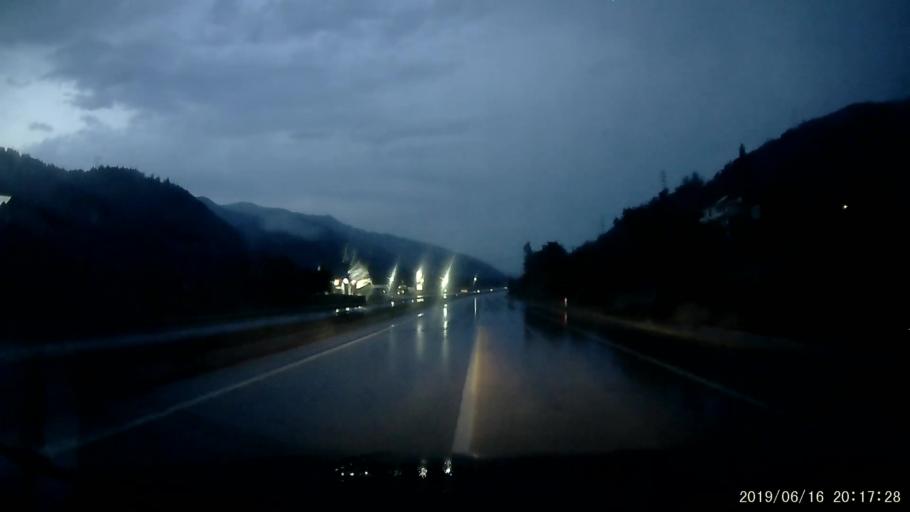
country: TR
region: Tokat
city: Resadiye
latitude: 40.3653
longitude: 37.4219
